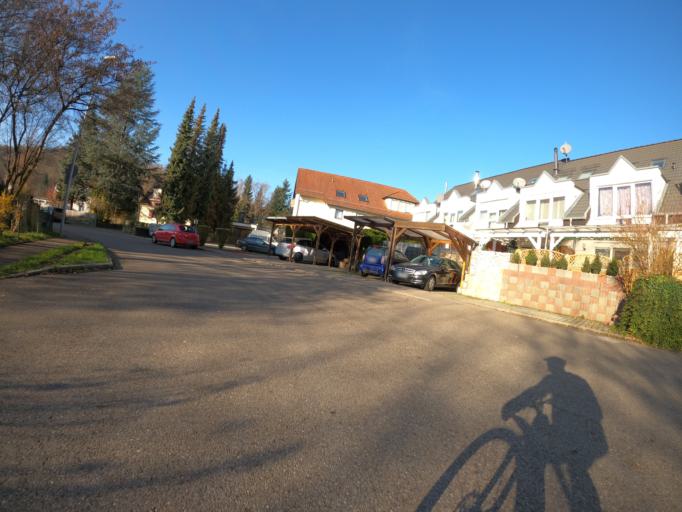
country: DE
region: Baden-Wuerttemberg
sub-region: Regierungsbezirk Stuttgart
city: Uhingen
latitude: 48.7053
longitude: 9.5761
